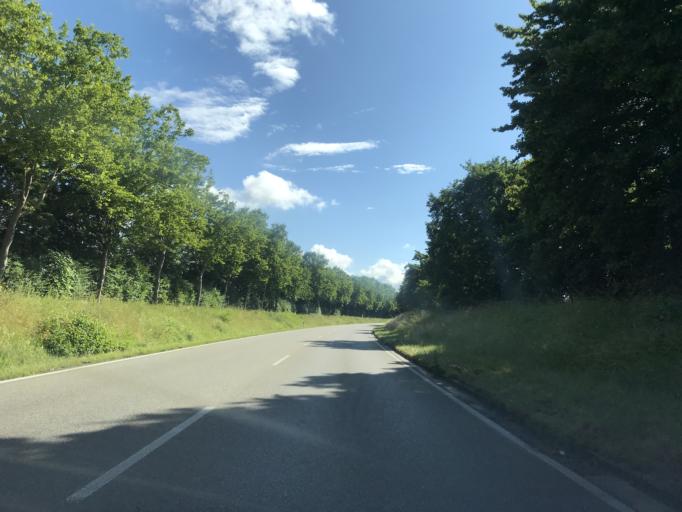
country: DE
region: Baden-Wuerttemberg
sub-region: Freiburg Region
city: Loerrach
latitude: 47.6307
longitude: 7.6671
